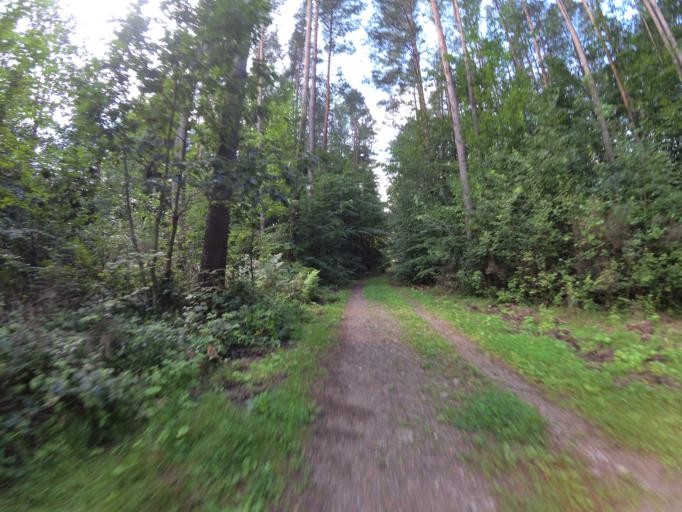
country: PL
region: Pomeranian Voivodeship
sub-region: Gdynia
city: Wielki Kack
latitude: 54.5032
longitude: 18.4373
